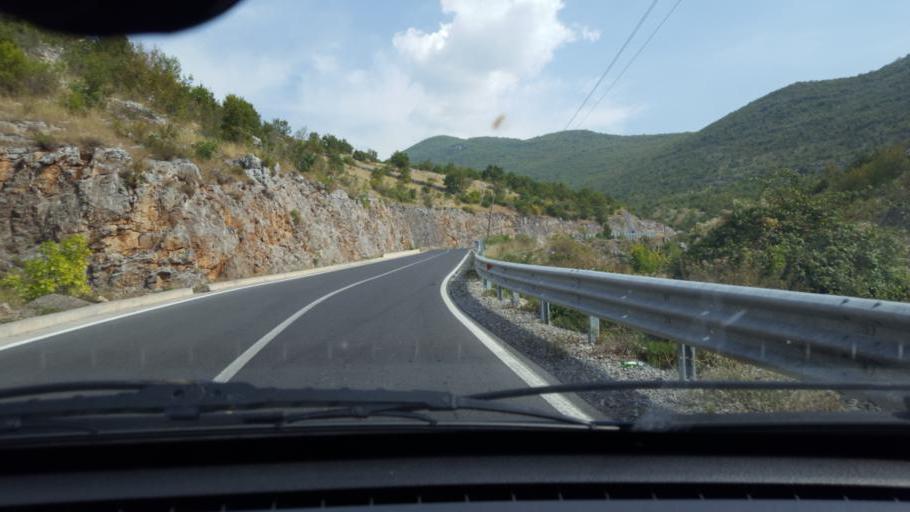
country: AL
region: Shkoder
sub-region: Rrethi i Malesia e Madhe
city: Hot
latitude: 42.3742
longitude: 19.4670
